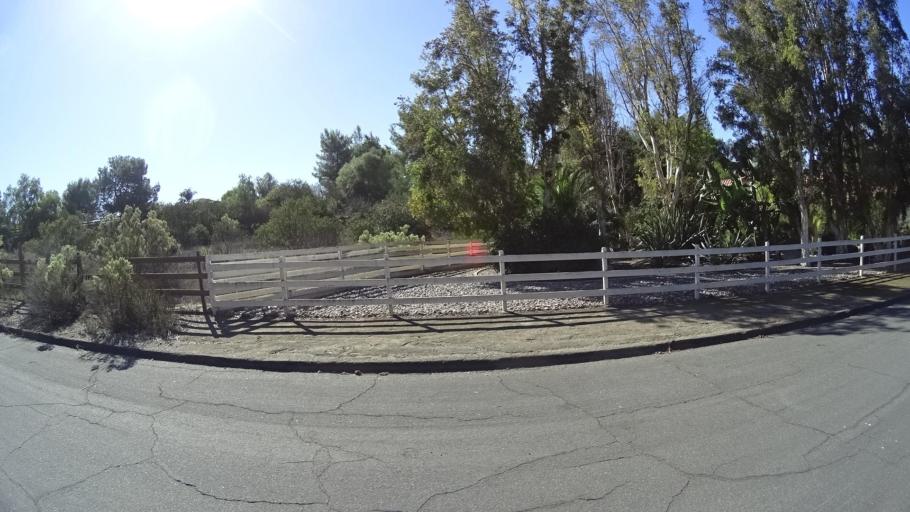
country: US
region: California
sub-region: San Diego County
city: Jamul
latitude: 32.7402
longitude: -116.8598
